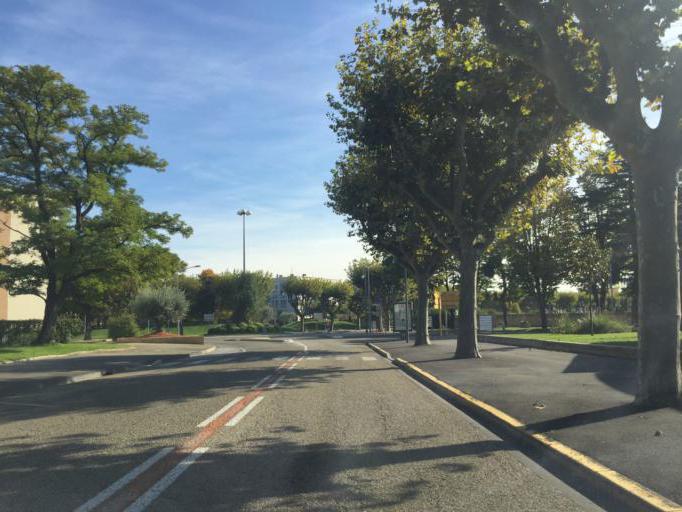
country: FR
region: Rhone-Alpes
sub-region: Departement de la Drome
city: Pierrelatte
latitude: 44.3795
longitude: 4.6989
